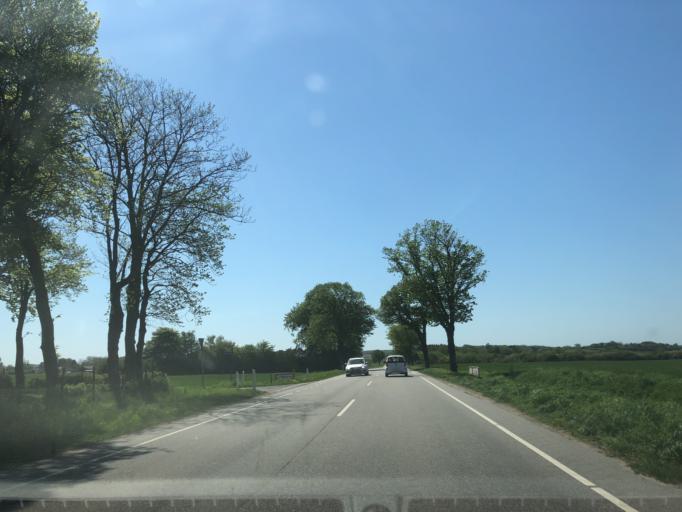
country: DK
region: Zealand
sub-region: Slagelse Kommune
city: Forlev
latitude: 55.3395
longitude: 11.2197
